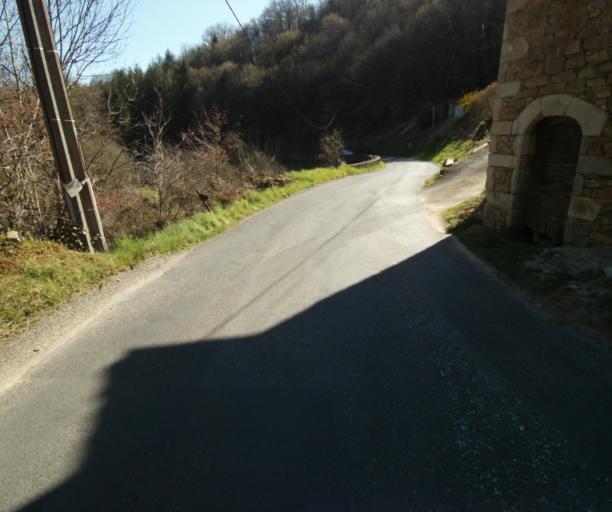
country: FR
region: Limousin
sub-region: Departement de la Correze
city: Tulle
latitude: 45.2736
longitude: 1.7382
